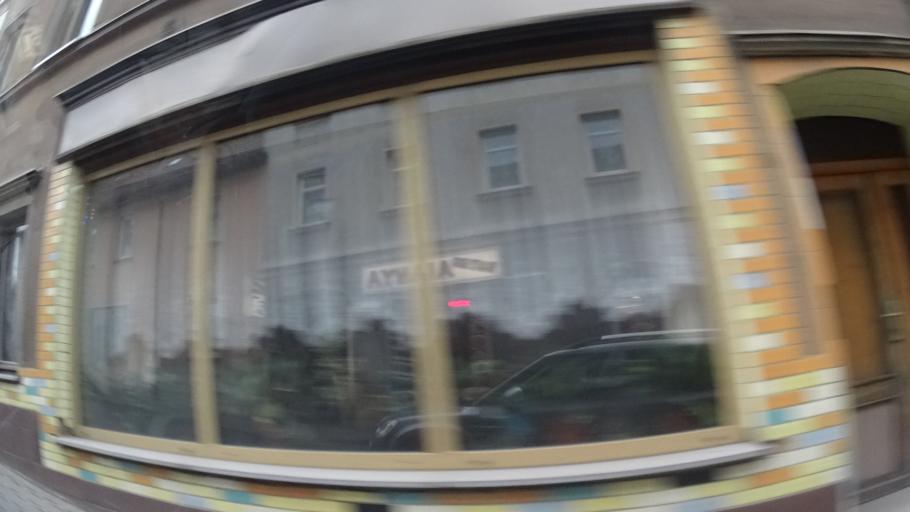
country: DE
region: Thuringia
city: Auma
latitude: 50.6999
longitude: 11.9010
